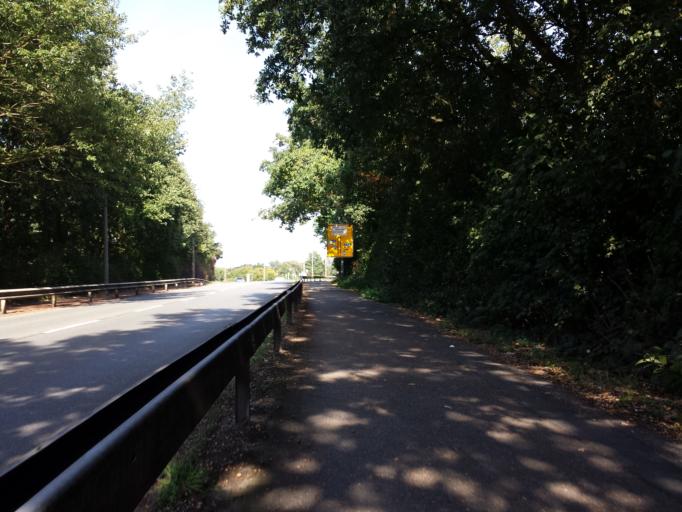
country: DE
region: Bremen
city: Bremen
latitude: 53.0388
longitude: 8.8394
